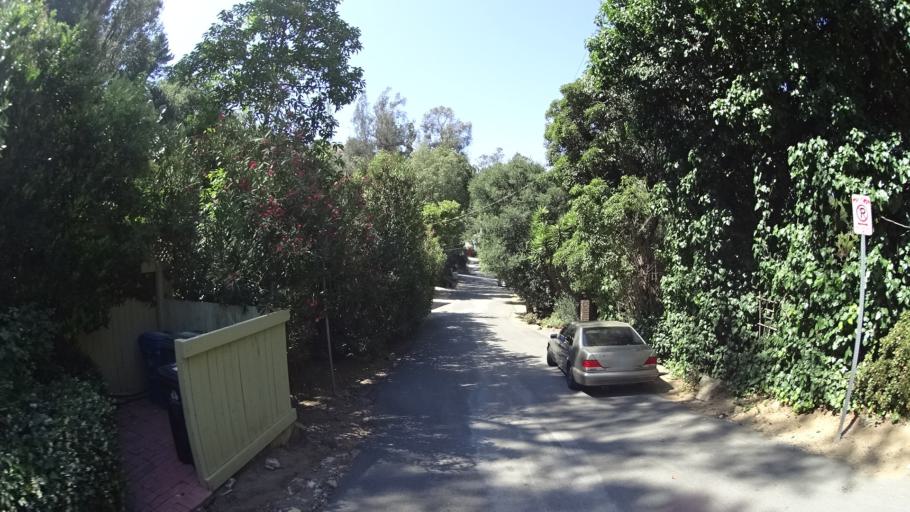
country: US
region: California
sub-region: Los Angeles County
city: West Hollywood
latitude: 34.1078
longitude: -118.3838
